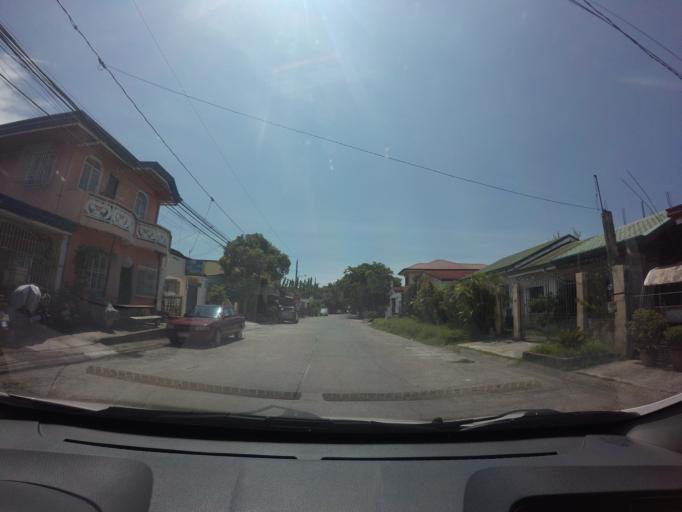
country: PH
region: Calabarzon
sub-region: Province of Rizal
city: Las Pinas
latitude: 14.4398
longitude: 120.9754
